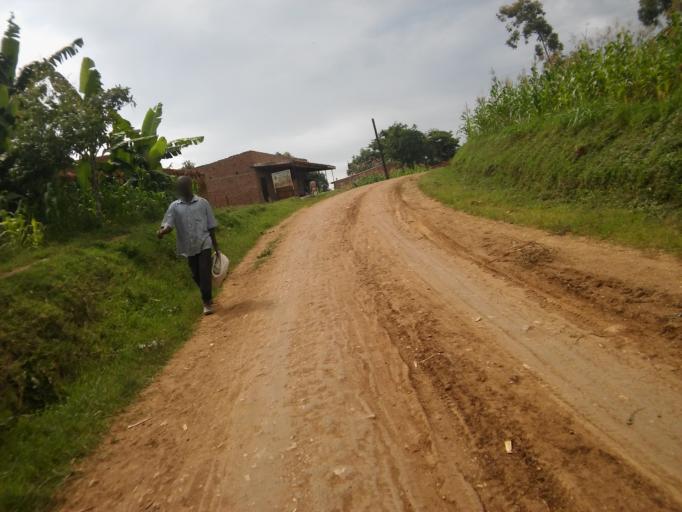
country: UG
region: Eastern Region
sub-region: Manafwa District
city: Manafwa
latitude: 0.9012
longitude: 34.3557
